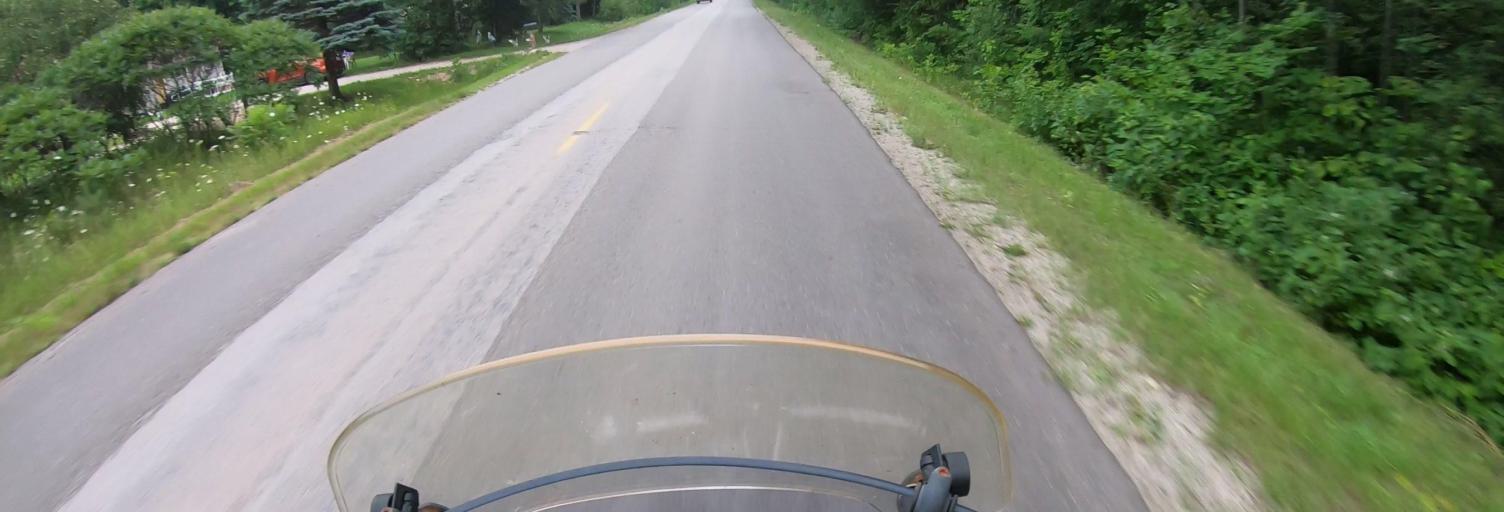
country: US
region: Michigan
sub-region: Mackinac County
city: Saint Ignace
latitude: 45.6945
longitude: -84.8207
